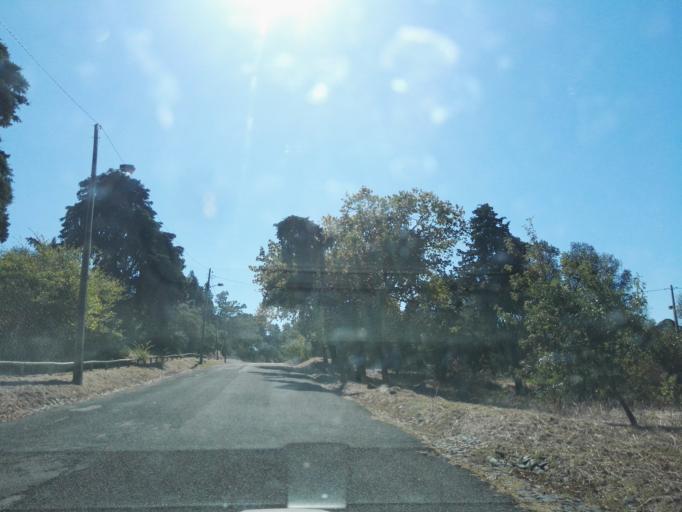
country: PT
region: Lisbon
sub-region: Oeiras
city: Alges
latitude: 38.7213
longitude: -9.1995
